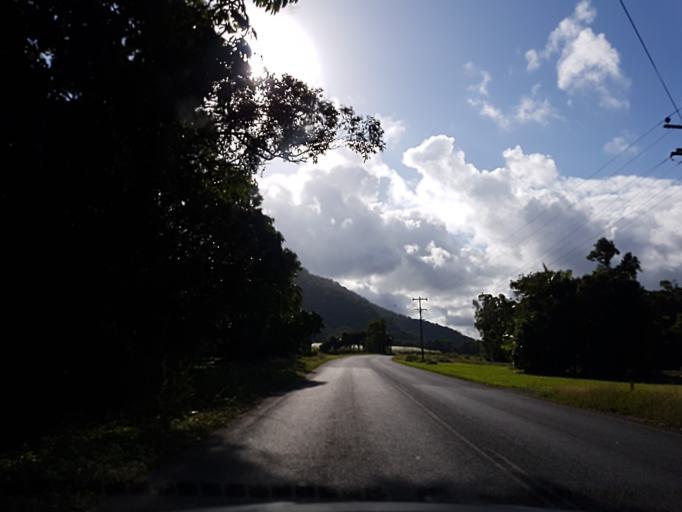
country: AU
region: Queensland
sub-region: Cairns
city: Port Douglas
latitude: -16.3061
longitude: 145.3912
